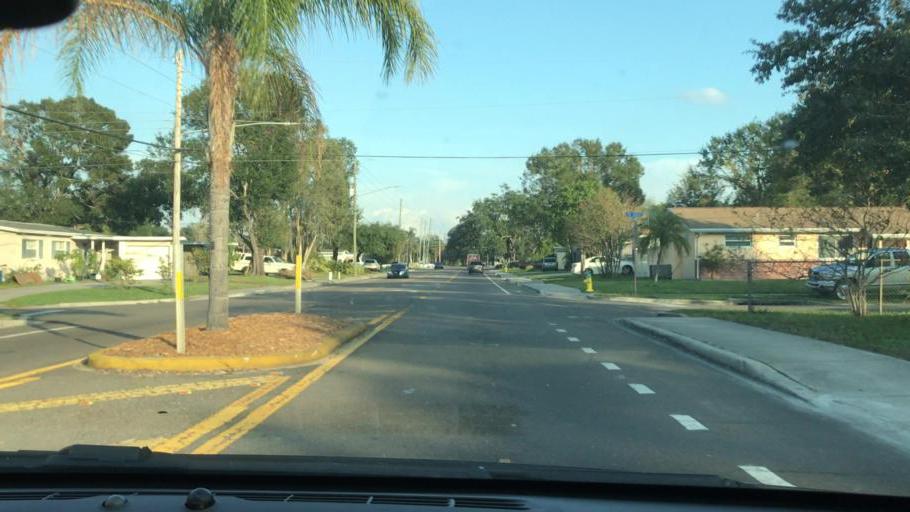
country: US
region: Florida
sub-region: Pinellas County
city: Pinellas Park
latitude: 27.8575
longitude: -82.7029
